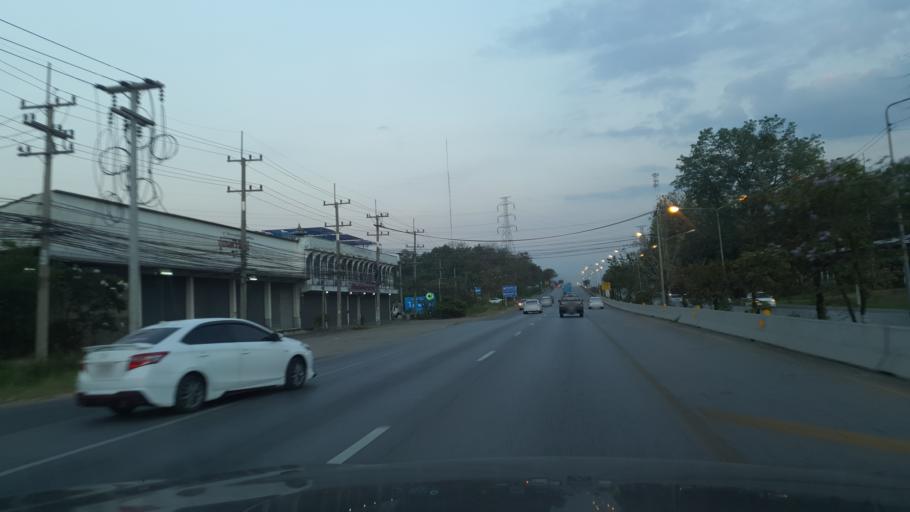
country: TH
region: Nakhon Sawan
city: Nakhon Sawan
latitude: 15.7072
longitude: 100.0956
